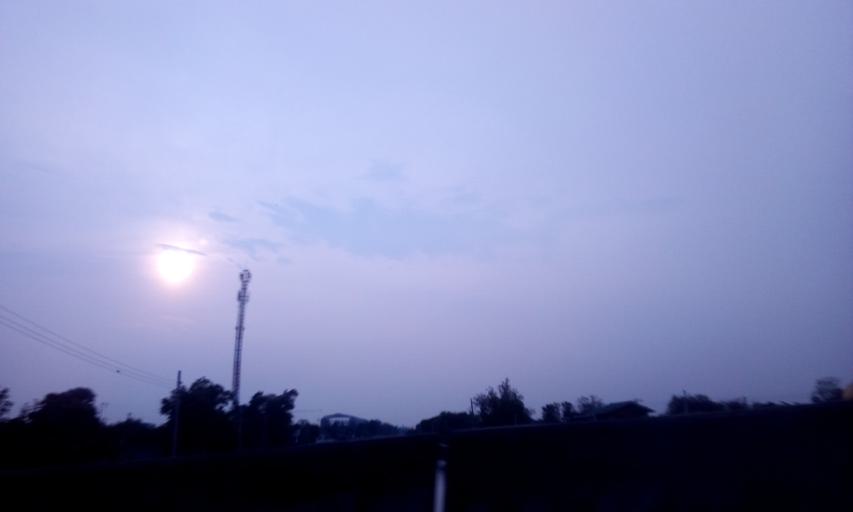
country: TH
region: Bangkok
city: Nong Chok
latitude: 13.8518
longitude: 100.8856
